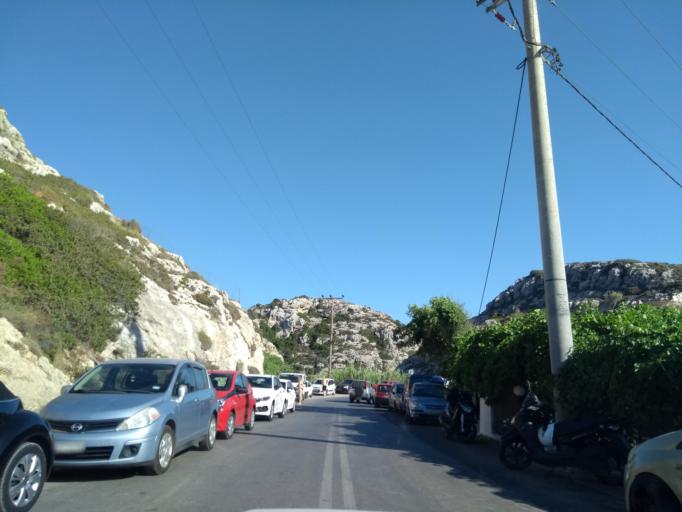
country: GR
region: Crete
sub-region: Nomos Chanias
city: Pithari
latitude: 35.5546
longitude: 24.0878
